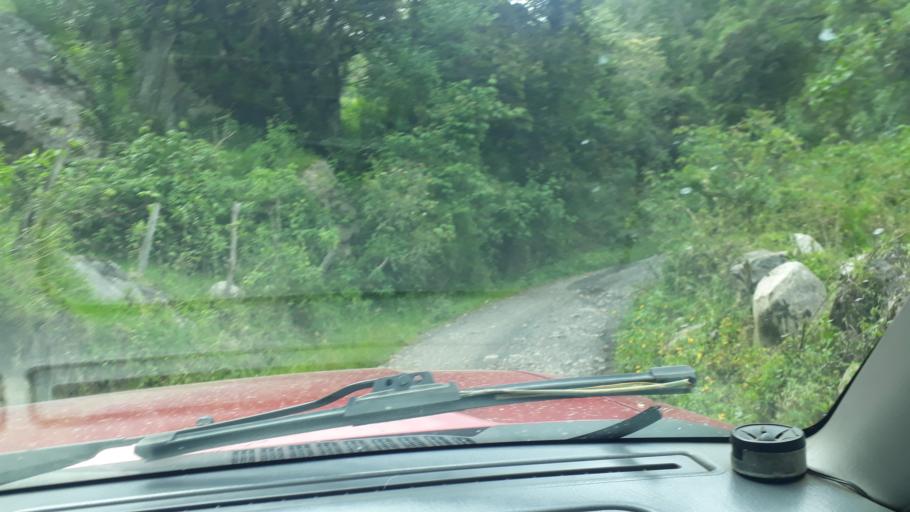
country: CO
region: Boyaca
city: San Mateo
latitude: 6.3974
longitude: -72.5418
